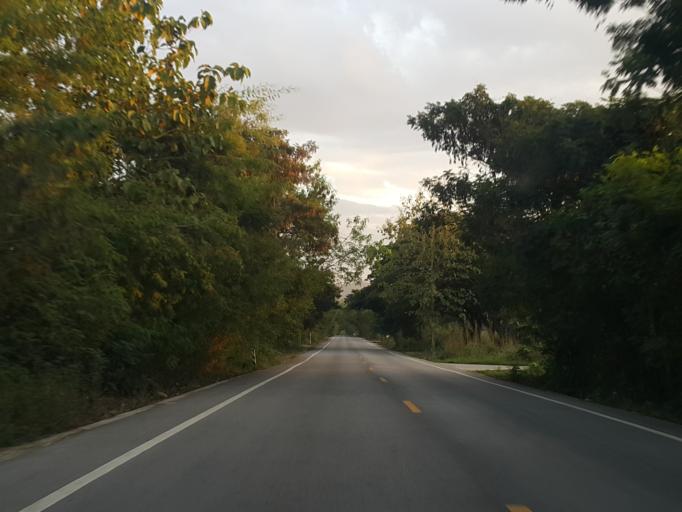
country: TH
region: Lampang
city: Mae Mo
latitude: 18.4312
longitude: 99.6429
